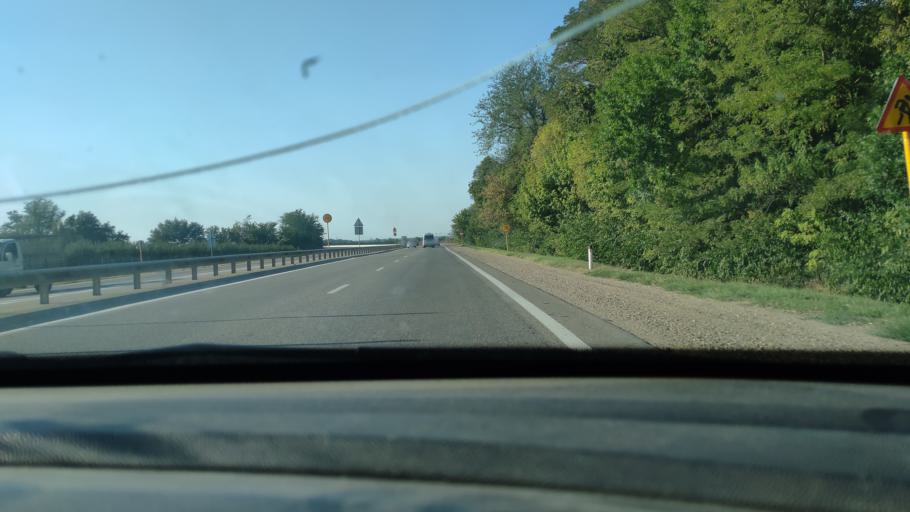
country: RU
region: Krasnodarskiy
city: Medvedovskaya
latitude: 45.4655
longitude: 38.9832
